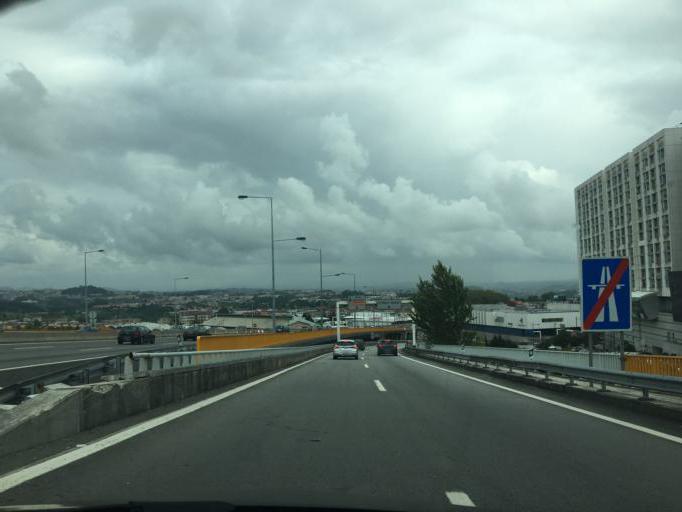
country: PT
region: Porto
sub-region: Maia
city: Pedroucos
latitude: 41.1659
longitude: -8.5833
